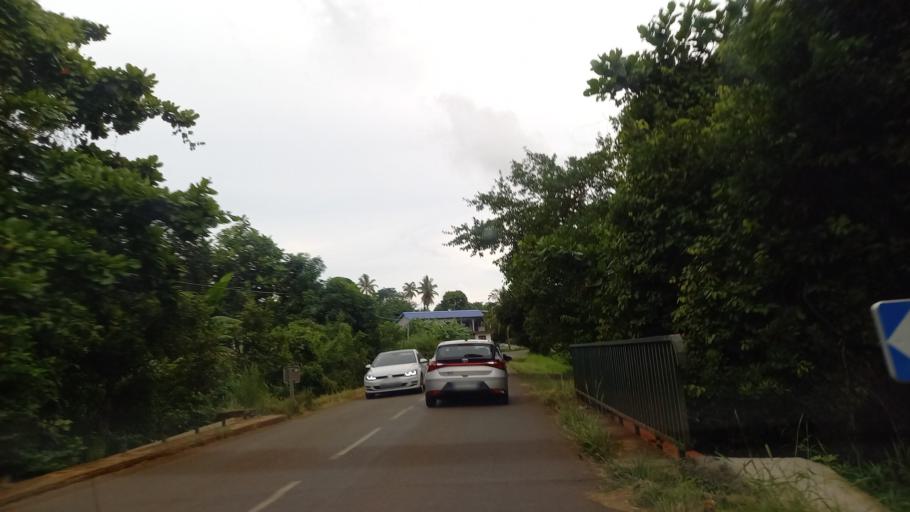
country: YT
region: Chirongui
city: Chirongui
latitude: -12.9029
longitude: 45.1499
